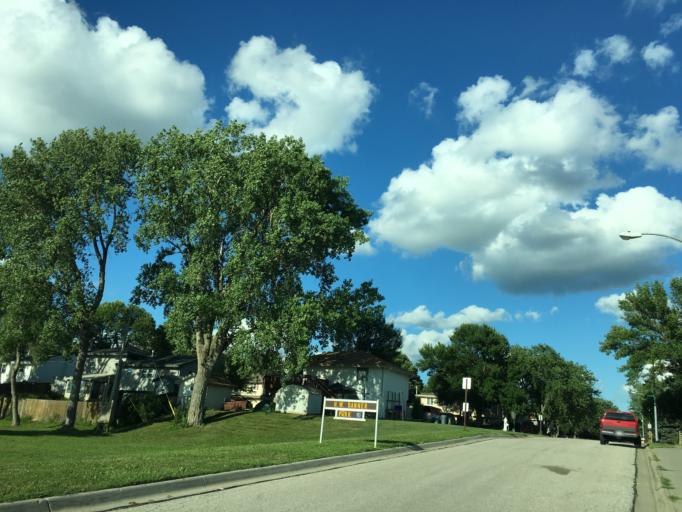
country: US
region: Nebraska
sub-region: Sarpy County
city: La Vista
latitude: 41.1743
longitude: -95.9928
